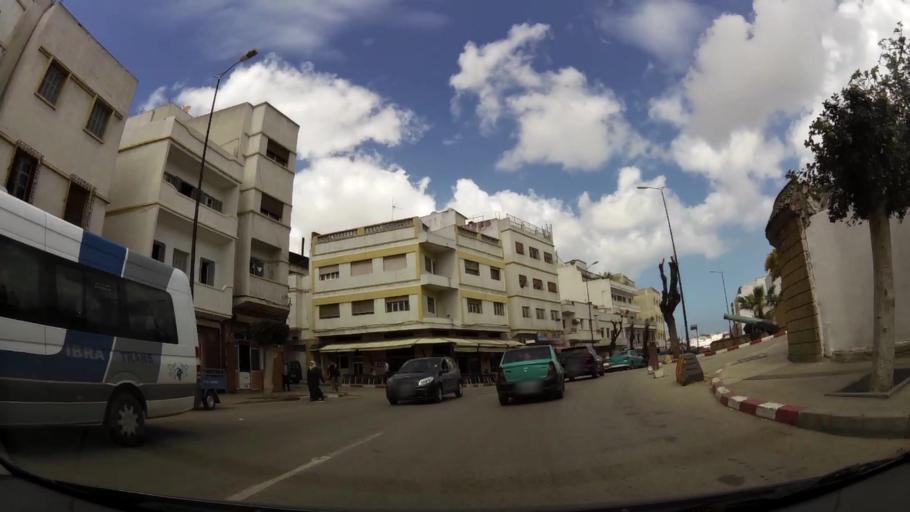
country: MA
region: Tanger-Tetouan
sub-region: Tanger-Assilah
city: Tangier
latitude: 35.7594
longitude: -5.8128
